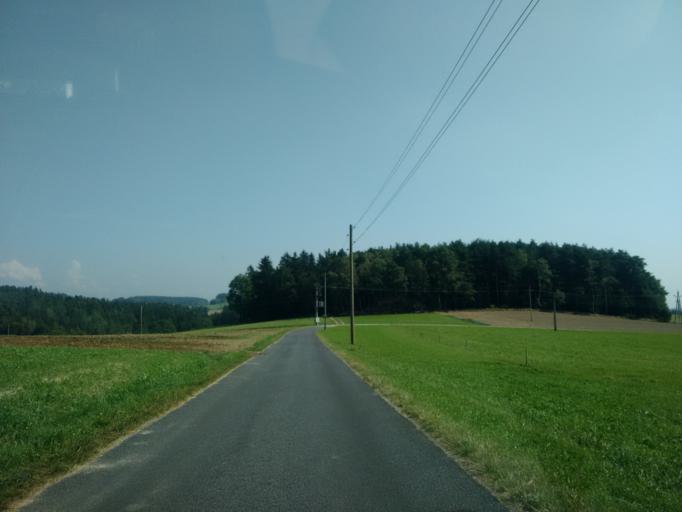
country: AT
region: Upper Austria
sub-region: Politischer Bezirk Urfahr-Umgebung
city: Haibach im Muhlkreis
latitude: 48.4110
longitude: 14.3549
